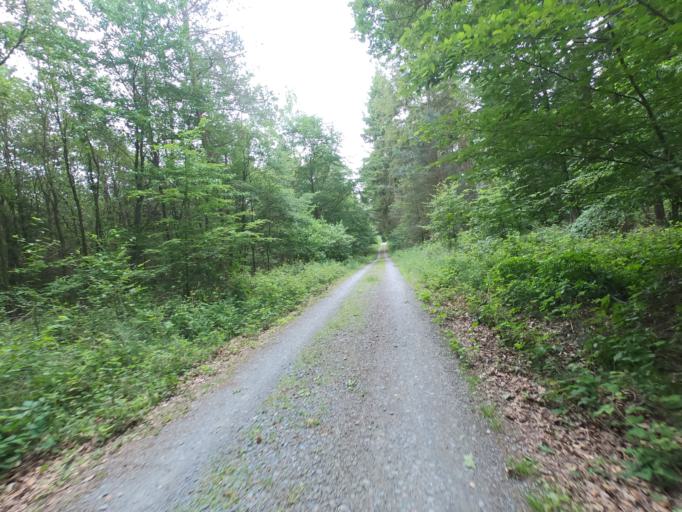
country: DE
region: Hesse
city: Langen
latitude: 50.0342
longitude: 8.6441
